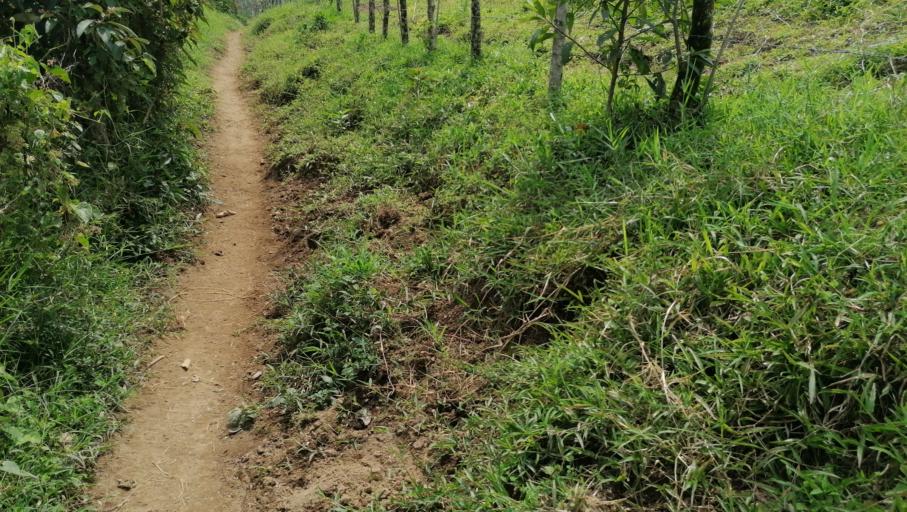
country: MX
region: Chiapas
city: Ocotepec
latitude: 17.2921
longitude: -93.2247
